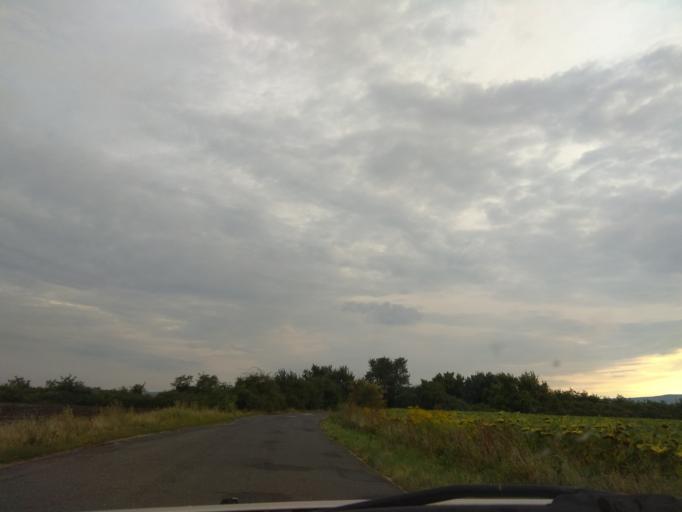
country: HU
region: Borsod-Abauj-Zemplen
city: Felsozsolca
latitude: 48.0805
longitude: 20.8450
